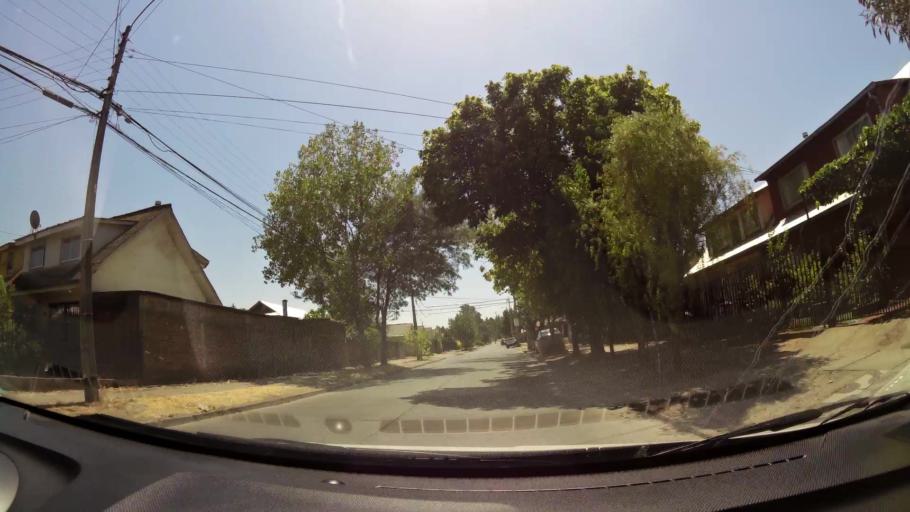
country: CL
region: Maule
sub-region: Provincia de Talca
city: Talca
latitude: -35.4237
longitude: -71.6288
